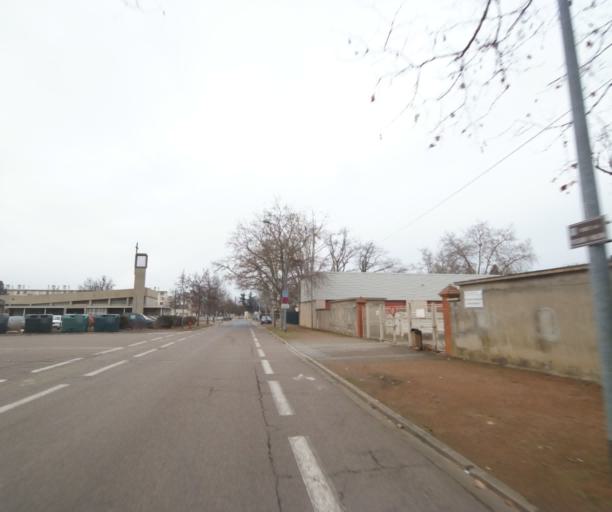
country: FR
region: Rhone-Alpes
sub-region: Departement de la Loire
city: Le Coteau
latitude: 46.0558
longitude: 4.0915
